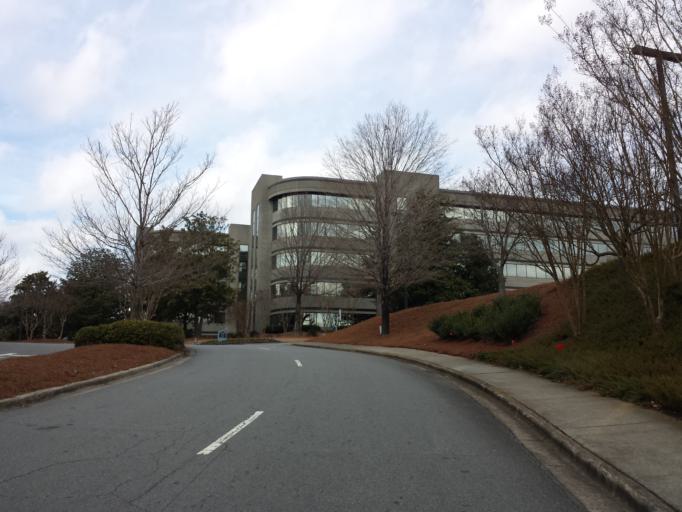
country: US
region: Georgia
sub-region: Cobb County
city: Vinings
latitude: 33.9049
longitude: -84.4678
